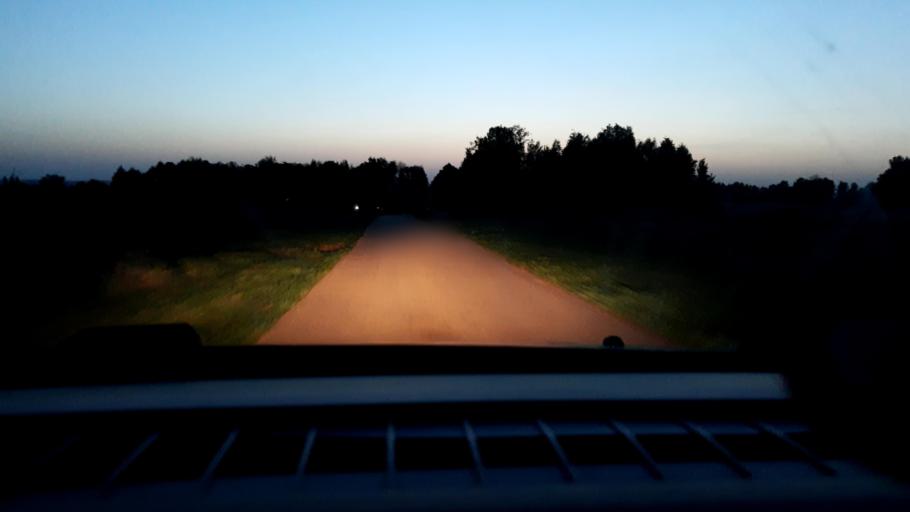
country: RU
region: Nizjnij Novgorod
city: Burevestnik
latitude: 56.0410
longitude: 43.7227
